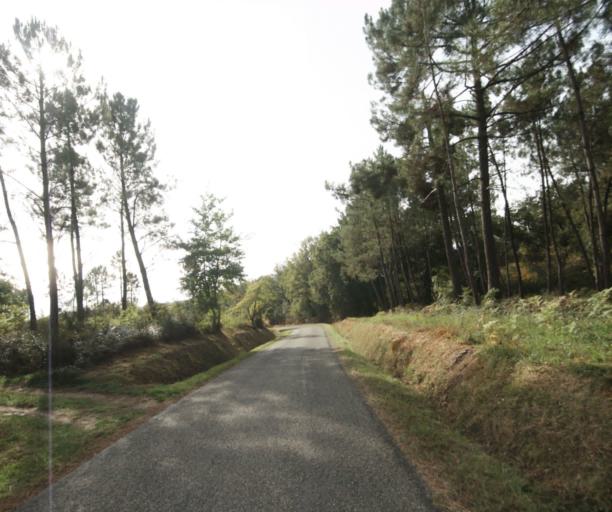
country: FR
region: Midi-Pyrenees
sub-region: Departement du Gers
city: Eauze
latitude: 43.9367
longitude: 0.1024
